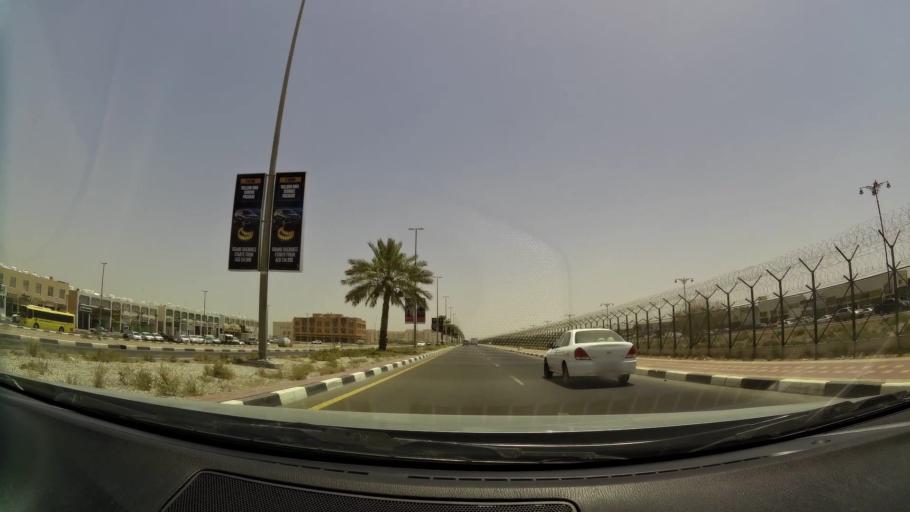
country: OM
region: Al Buraimi
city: Al Buraymi
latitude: 24.2644
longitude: 55.7708
